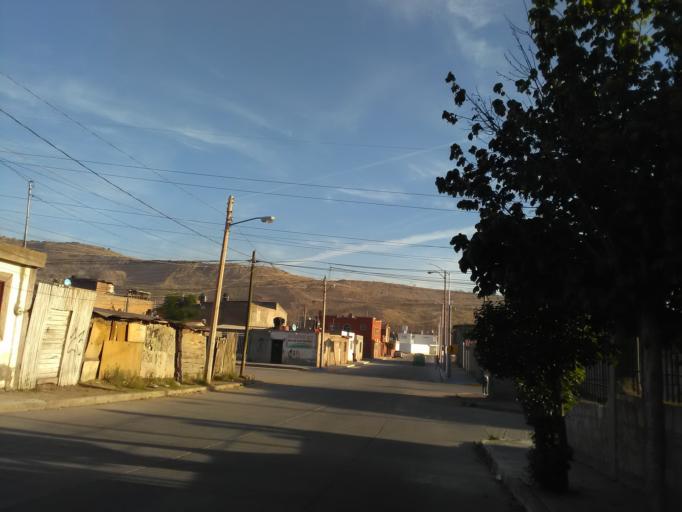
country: MX
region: Durango
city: Victoria de Durango
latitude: 24.0463
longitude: -104.6652
